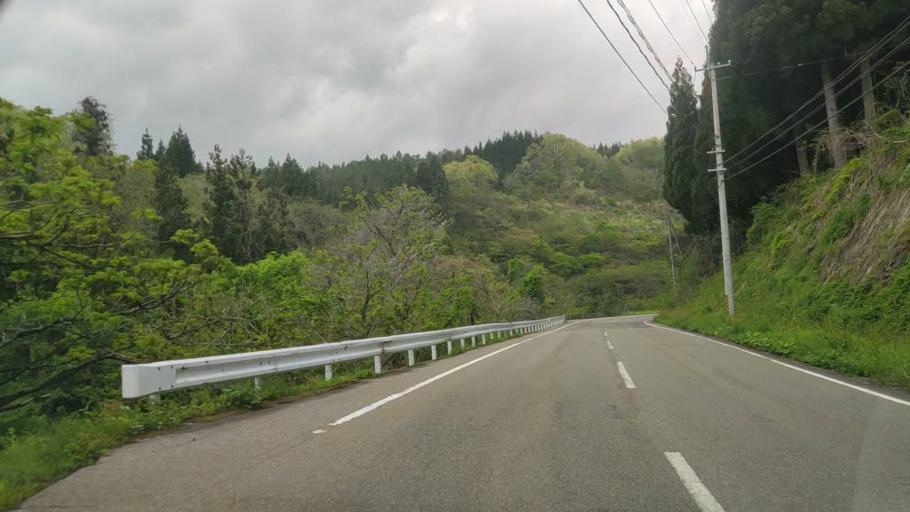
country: JP
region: Fukushima
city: Kitakata
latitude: 37.6595
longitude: 139.5886
